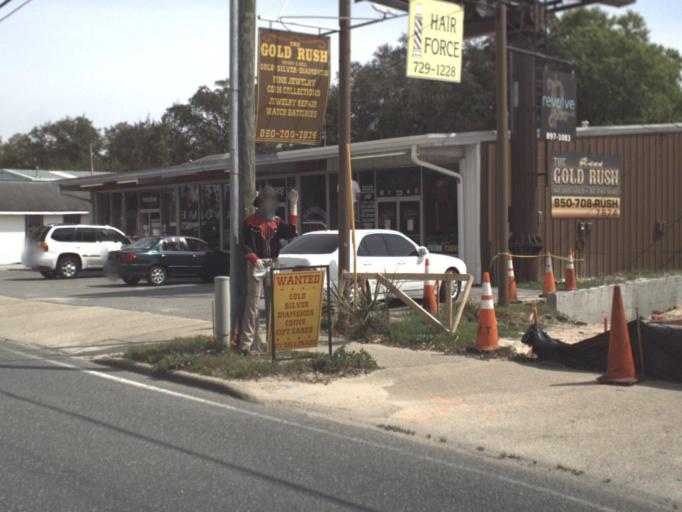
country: US
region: Florida
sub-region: Okaloosa County
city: Niceville
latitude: 30.5190
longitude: -86.4798
